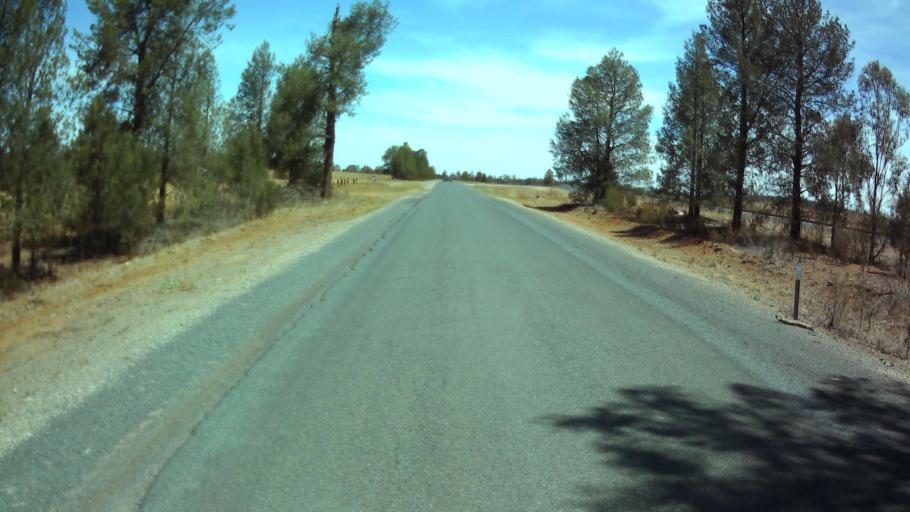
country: AU
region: New South Wales
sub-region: Weddin
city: Grenfell
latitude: -33.7721
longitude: 147.7564
